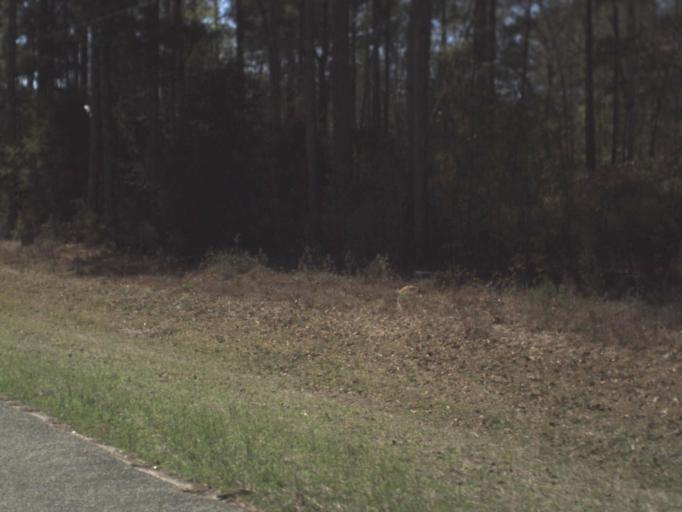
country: US
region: Florida
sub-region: Calhoun County
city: Blountstown
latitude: 30.5412
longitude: -85.0273
